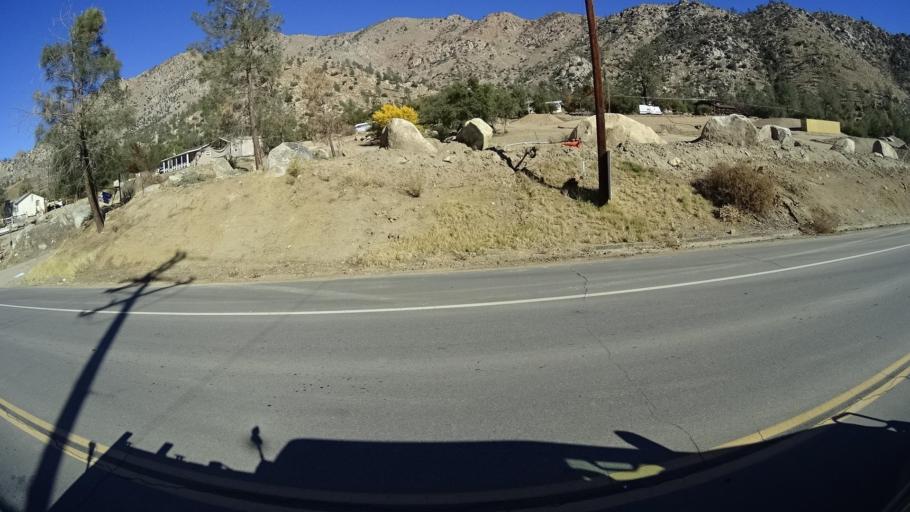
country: US
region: California
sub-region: Kern County
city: Kernville
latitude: 35.7549
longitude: -118.4188
